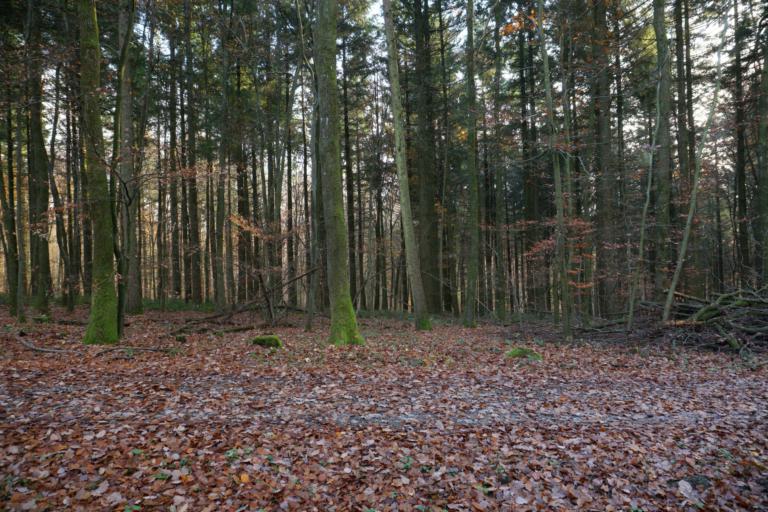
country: DE
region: Baden-Wuerttemberg
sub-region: Karlsruhe Region
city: Binau
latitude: 49.3231
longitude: 9.0371
